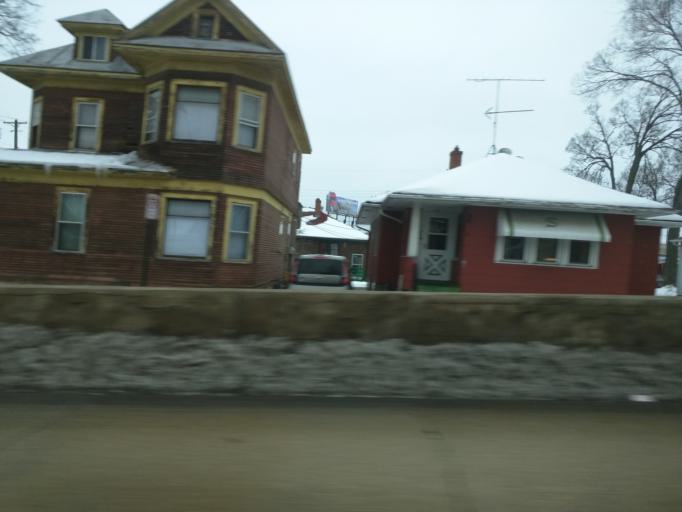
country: US
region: Wisconsin
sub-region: La Crosse County
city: North La Crosse
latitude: 43.8315
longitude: -91.2481
